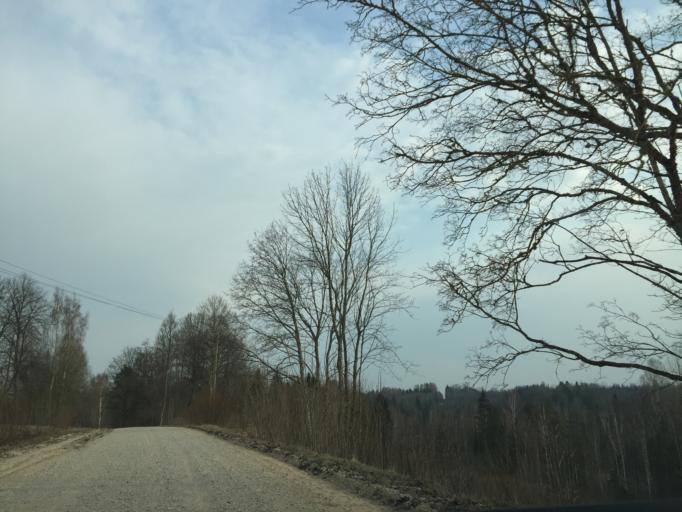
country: LV
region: Raunas
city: Rauna
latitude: 57.1560
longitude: 25.5778
